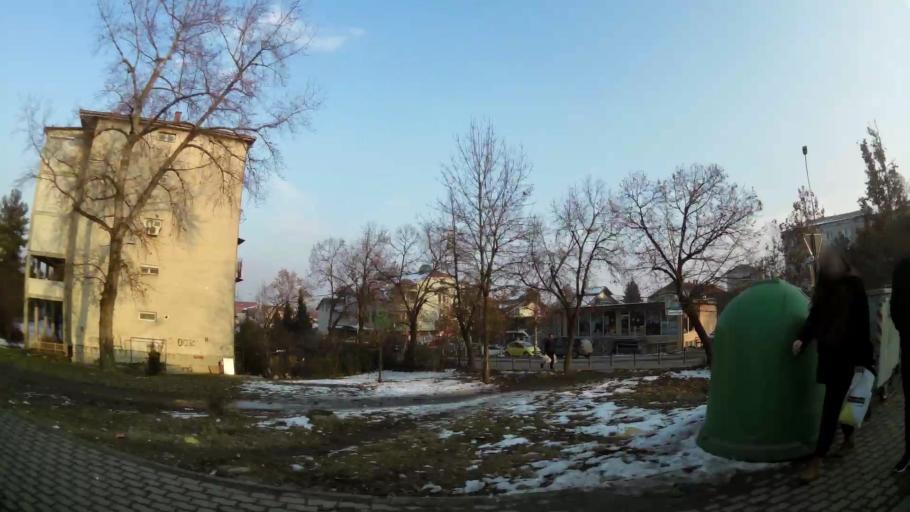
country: MK
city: Creshevo
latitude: 42.0114
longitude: 21.5094
